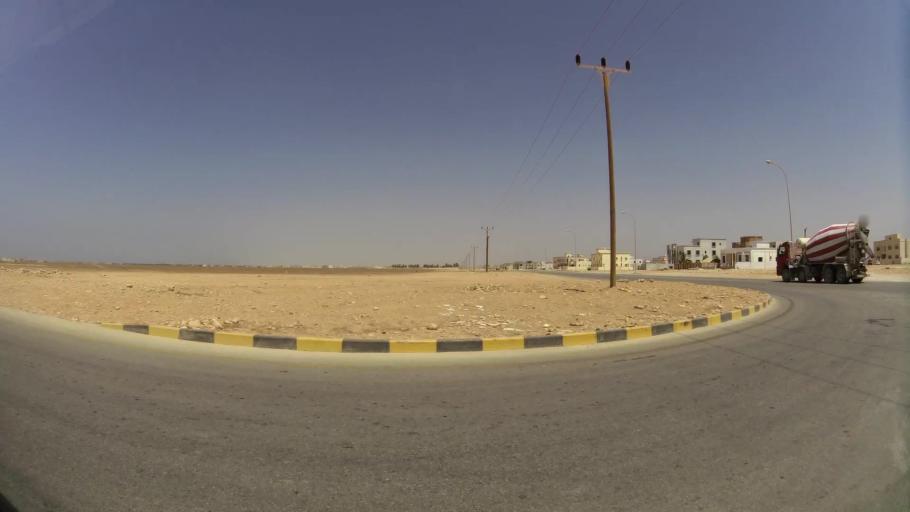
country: OM
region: Zufar
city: Salalah
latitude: 17.0682
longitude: 54.2106
